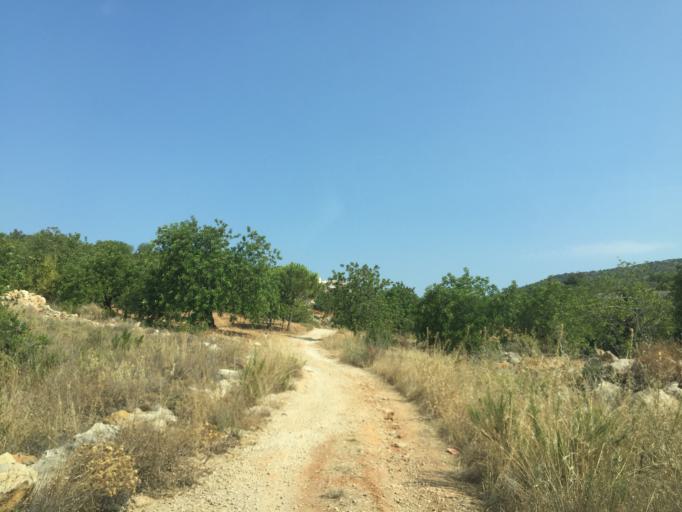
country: PT
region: Faro
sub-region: Loule
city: Almancil
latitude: 37.1028
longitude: -8.0051
